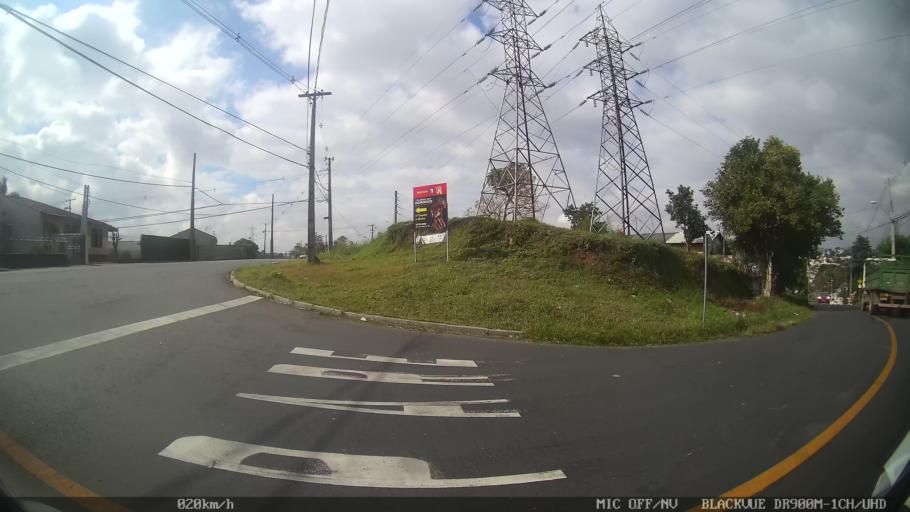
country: BR
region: Parana
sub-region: Curitiba
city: Curitiba
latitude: -25.3741
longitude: -49.2560
